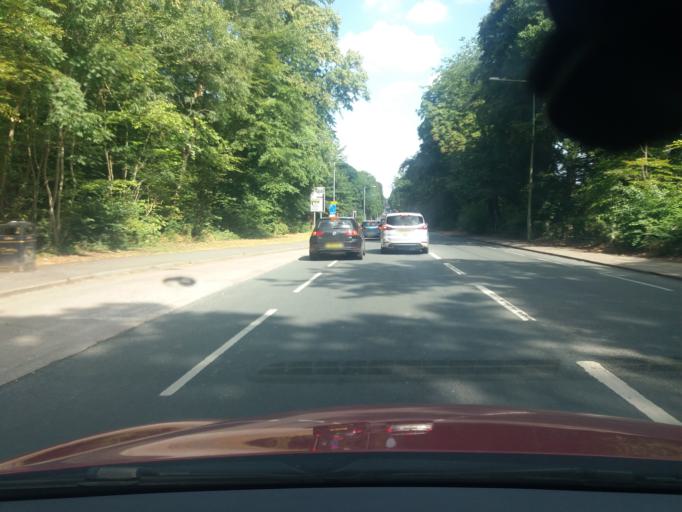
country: GB
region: England
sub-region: Lancashire
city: Chorley
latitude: 53.6374
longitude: -2.6163
